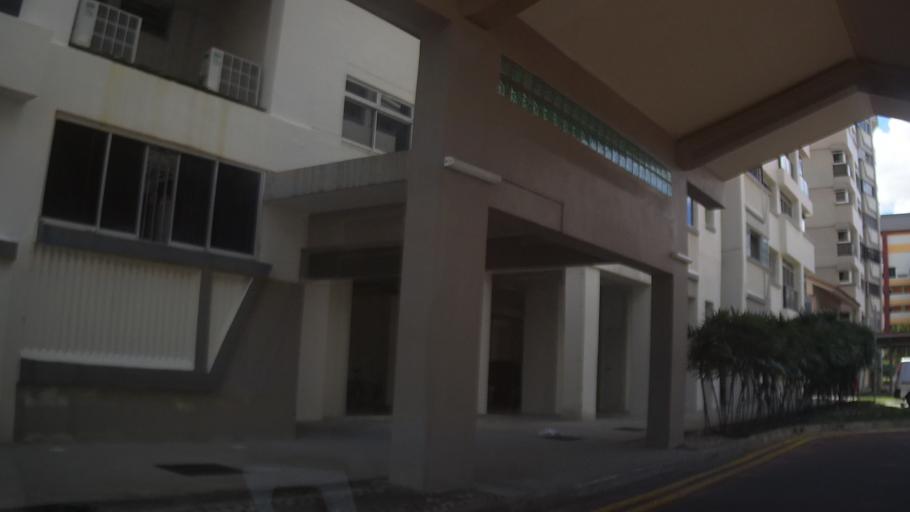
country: MY
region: Johor
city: Johor Bahru
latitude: 1.4329
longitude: 103.7842
